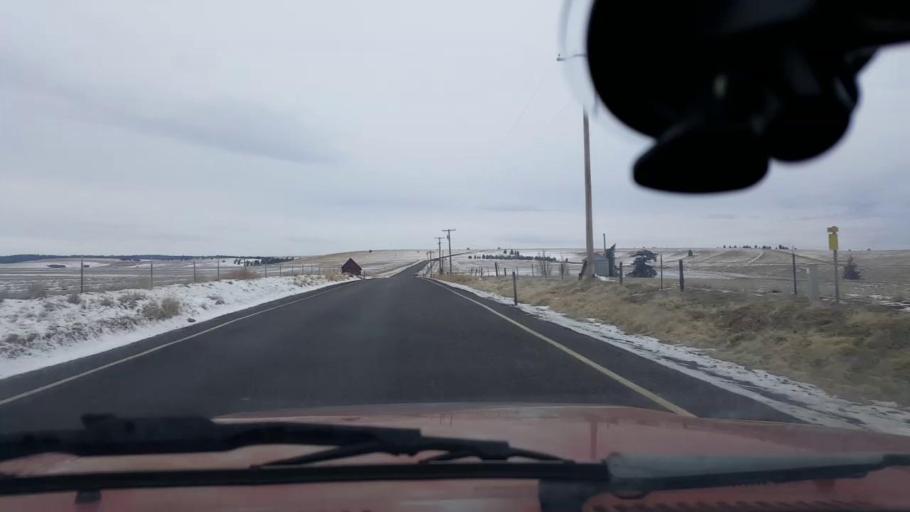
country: US
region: Washington
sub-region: Garfield County
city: Pomeroy
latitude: 46.3205
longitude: -117.3891
